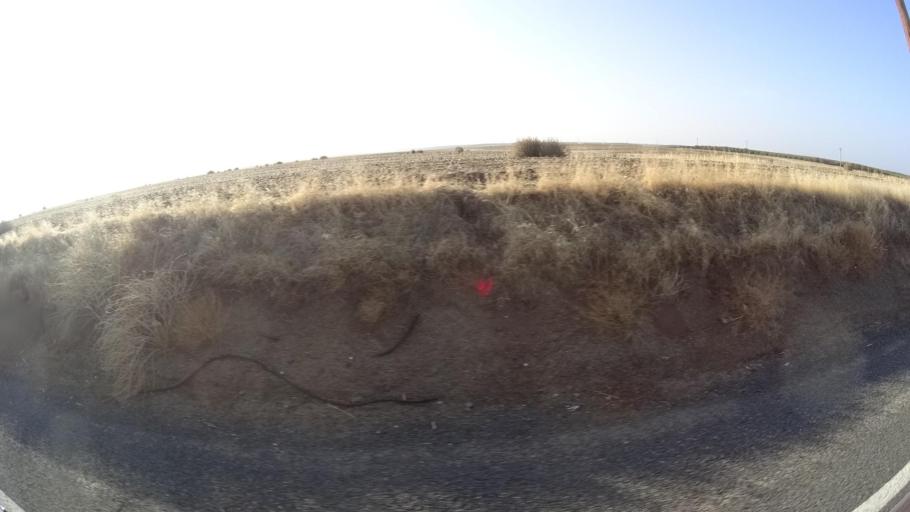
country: US
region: California
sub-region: Tulare County
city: Richgrove
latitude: 35.7619
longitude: -119.0782
